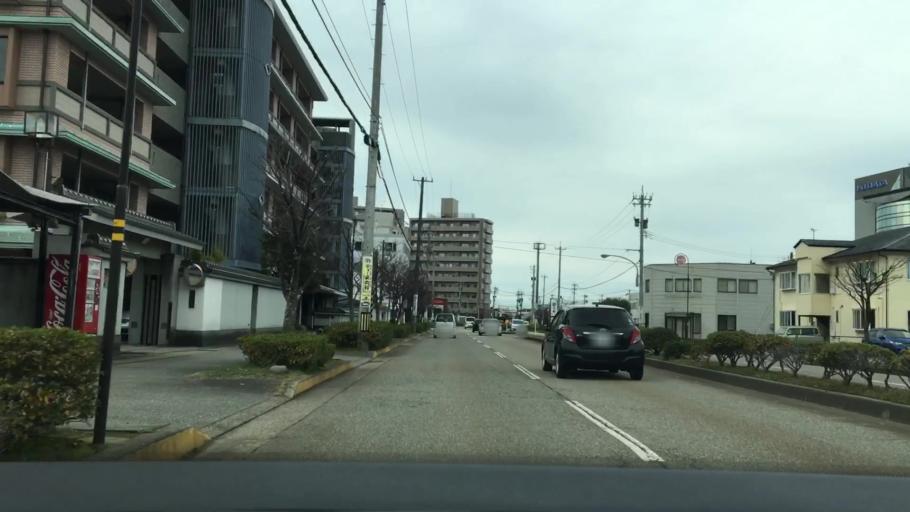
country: JP
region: Ishikawa
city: Kanazawa-shi
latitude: 36.5759
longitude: 136.6233
